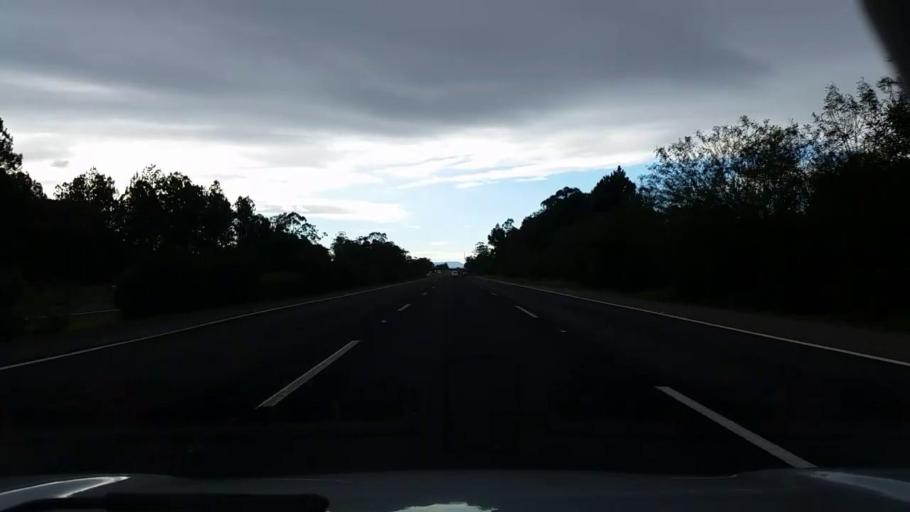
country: BR
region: Rio Grande do Sul
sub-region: Taquara
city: Taquara
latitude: -29.8901
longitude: -50.6988
